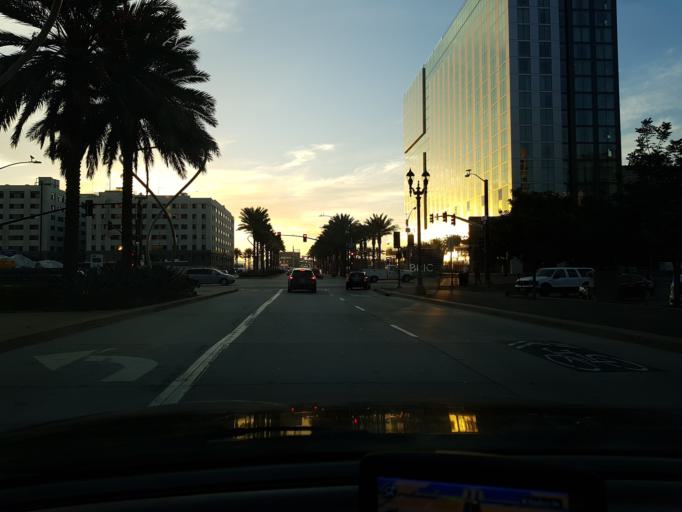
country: US
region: California
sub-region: San Diego County
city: San Diego
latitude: 32.7158
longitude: -117.1703
